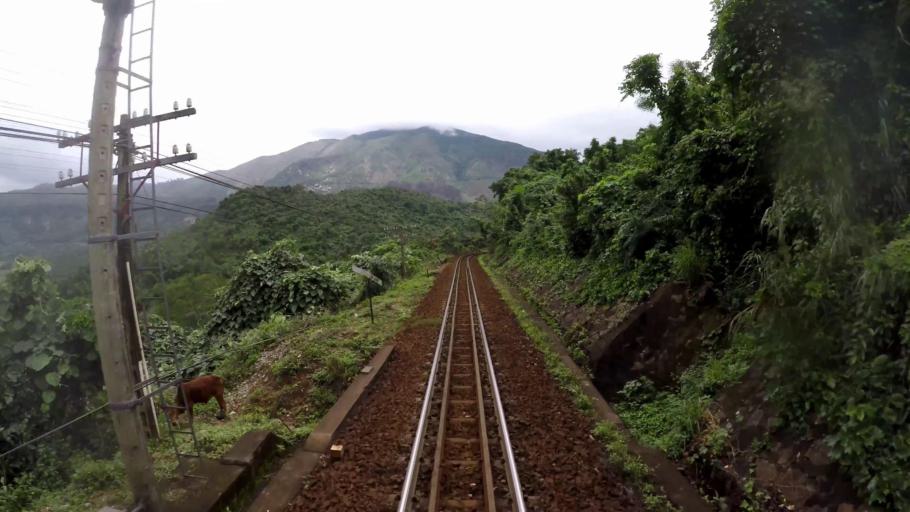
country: VN
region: Da Nang
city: Lien Chieu
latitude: 16.1708
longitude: 108.1466
